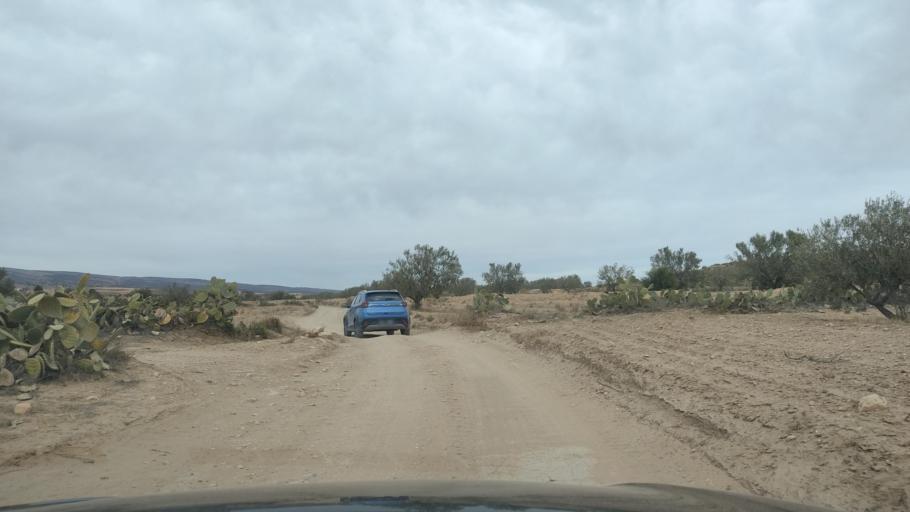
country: TN
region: Al Qasrayn
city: Kasserine
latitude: 35.2520
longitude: 8.9218
